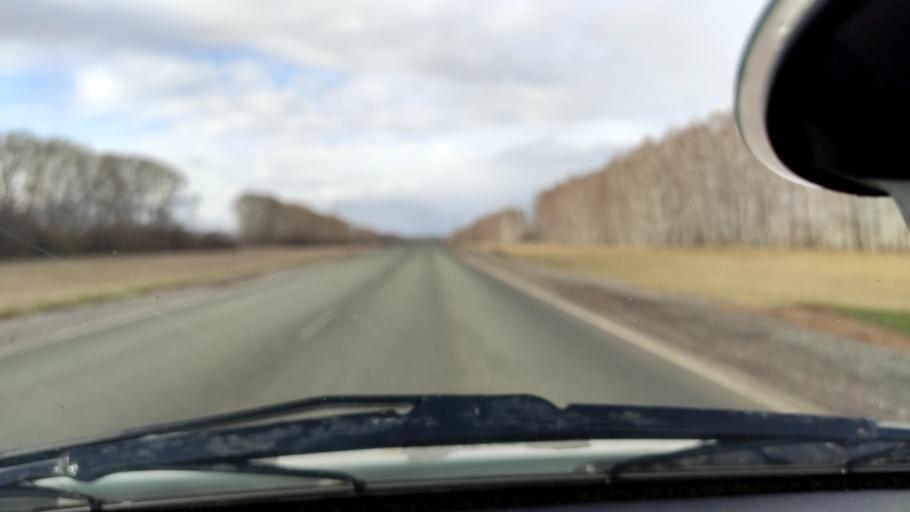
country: RU
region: Bashkortostan
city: Buzdyak
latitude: 54.6529
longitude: 54.5397
